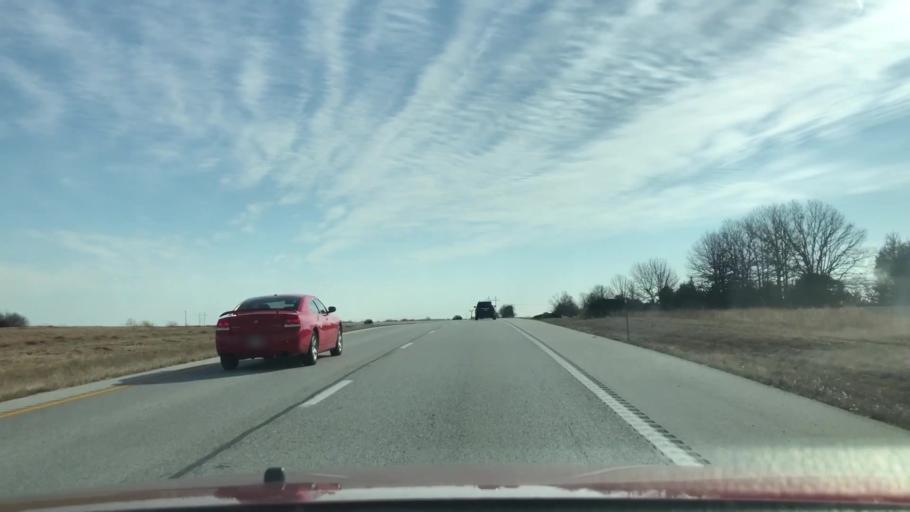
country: US
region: Missouri
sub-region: Webster County
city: Seymour
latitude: 37.1197
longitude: -92.6958
